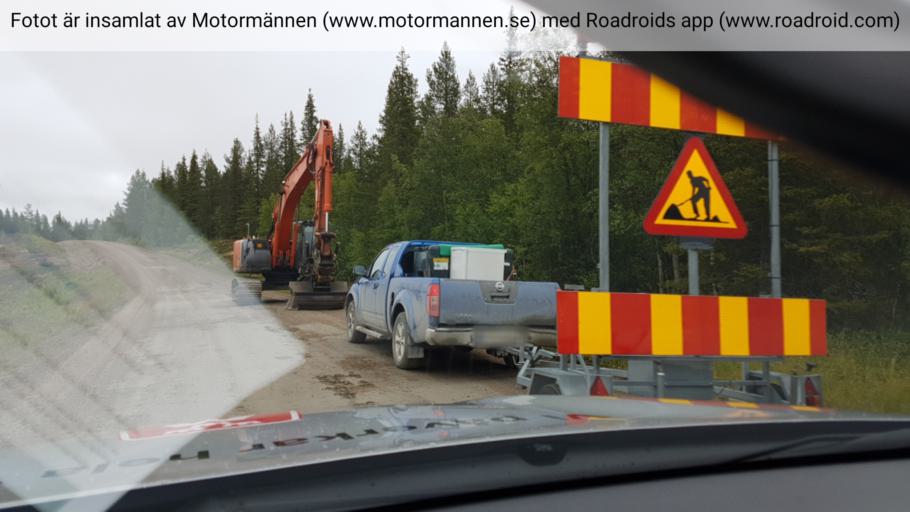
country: SE
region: Norrbotten
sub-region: Gallivare Kommun
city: Gaellivare
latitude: 66.7439
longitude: 20.6006
